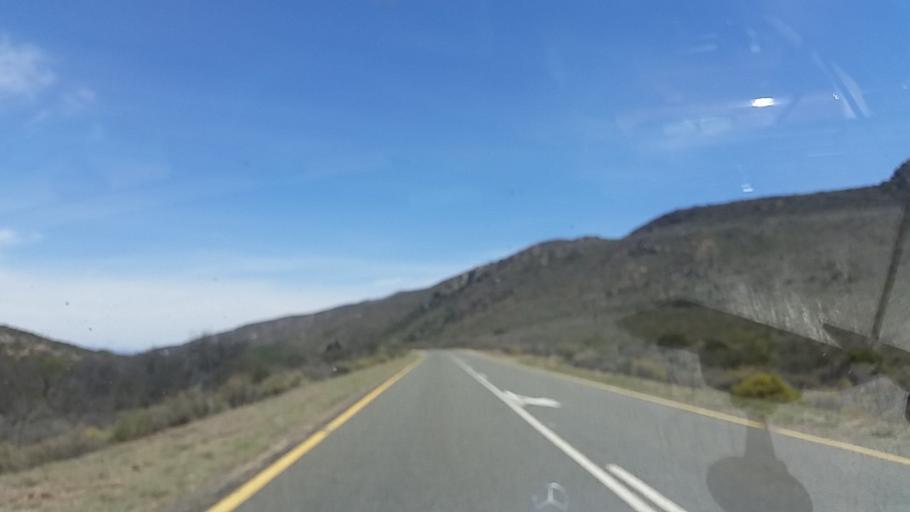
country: ZA
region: Eastern Cape
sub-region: Cacadu District Municipality
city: Willowmore
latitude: -33.3882
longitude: 23.3851
